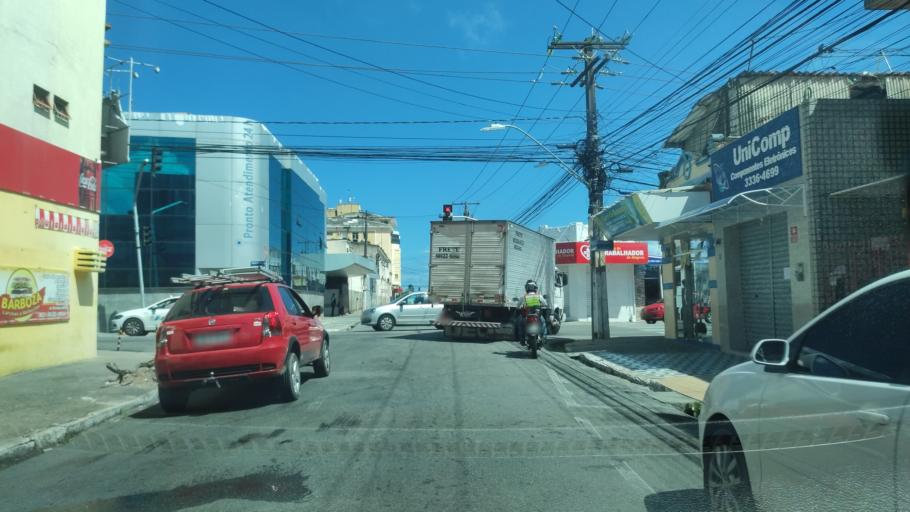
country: BR
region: Alagoas
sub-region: Maceio
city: Maceio
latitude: -9.6669
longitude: -35.7419
